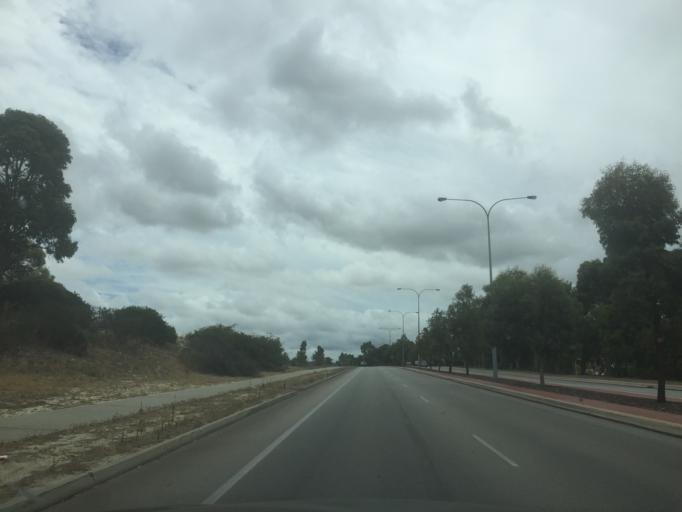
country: AU
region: Western Australia
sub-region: Gosnells
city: Thornlie
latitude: -32.0821
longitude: 115.9510
